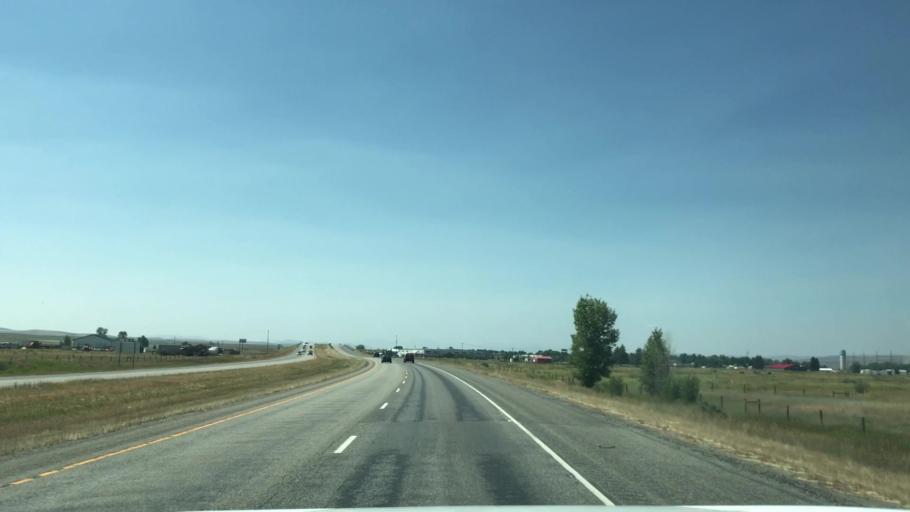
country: US
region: Montana
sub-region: Gallatin County
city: Manhattan
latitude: 45.8470
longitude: -111.3167
